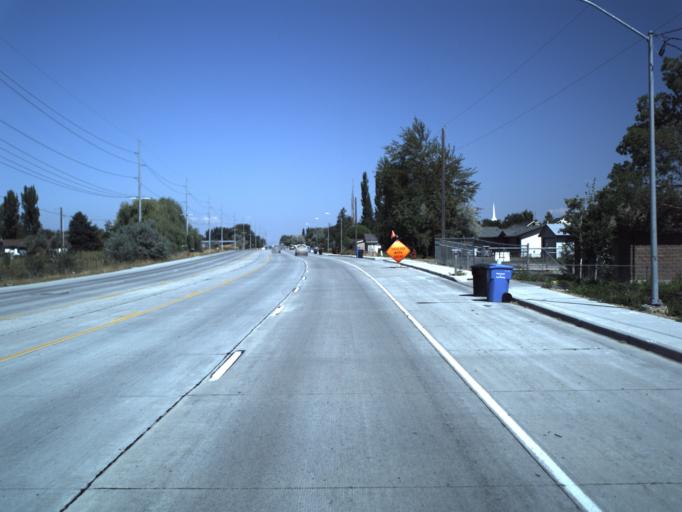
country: US
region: Utah
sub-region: Cache County
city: Logan
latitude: 41.7098
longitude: -111.8602
